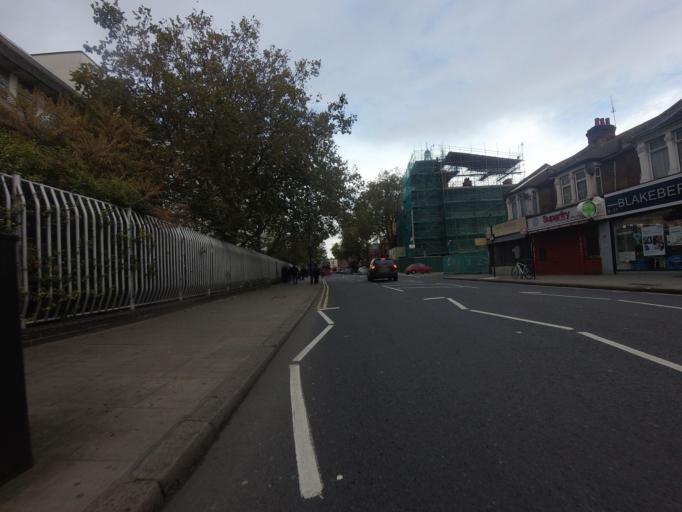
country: GB
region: England
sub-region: Greater London
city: East Ham
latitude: 51.5315
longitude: 0.0554
